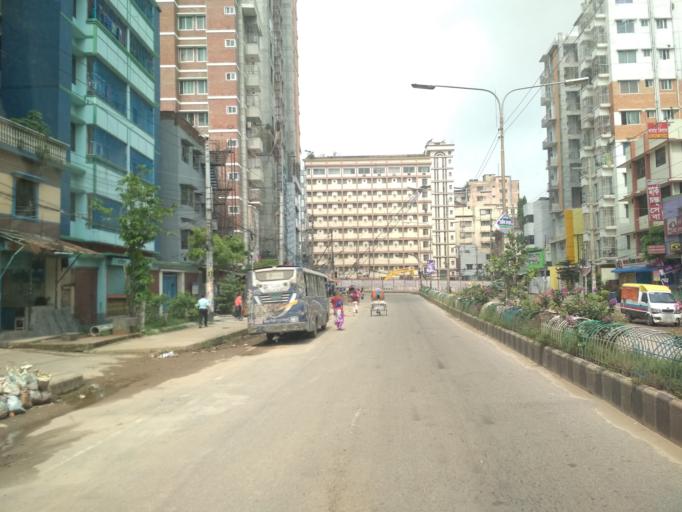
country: BD
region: Dhaka
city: Tungi
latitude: 23.8204
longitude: 90.3661
